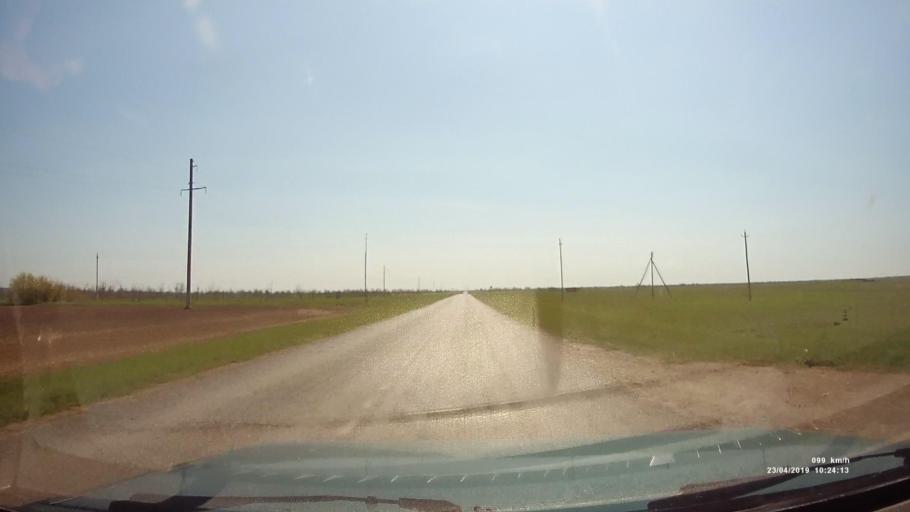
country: RU
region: Rostov
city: Sovetskoye
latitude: 46.6408
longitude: 42.4378
